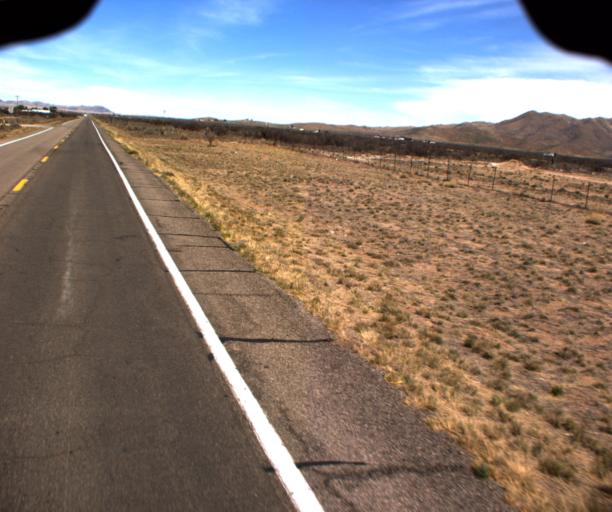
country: US
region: Arizona
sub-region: Cochise County
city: Willcox
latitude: 32.2814
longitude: -109.8125
